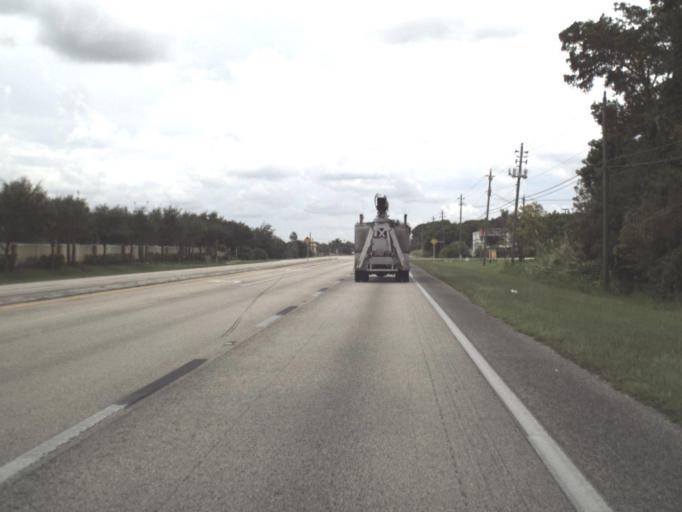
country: US
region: Florida
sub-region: Lee County
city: Olga
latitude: 26.7121
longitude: -81.7105
